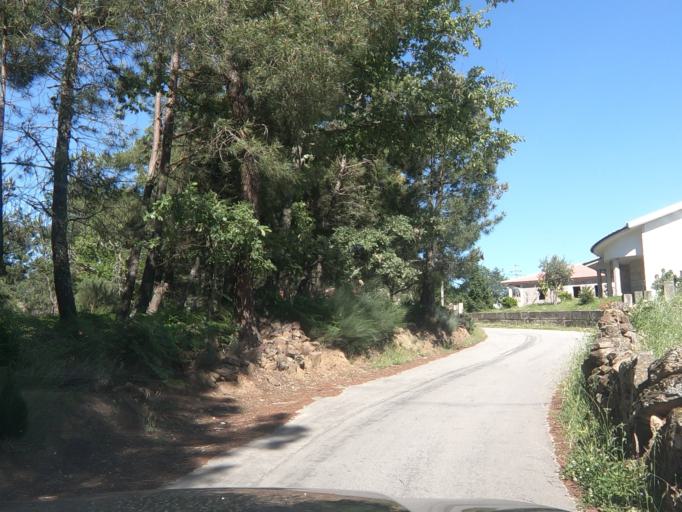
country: PT
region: Vila Real
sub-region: Vila Real
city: Vila Real
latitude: 41.3006
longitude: -7.6614
